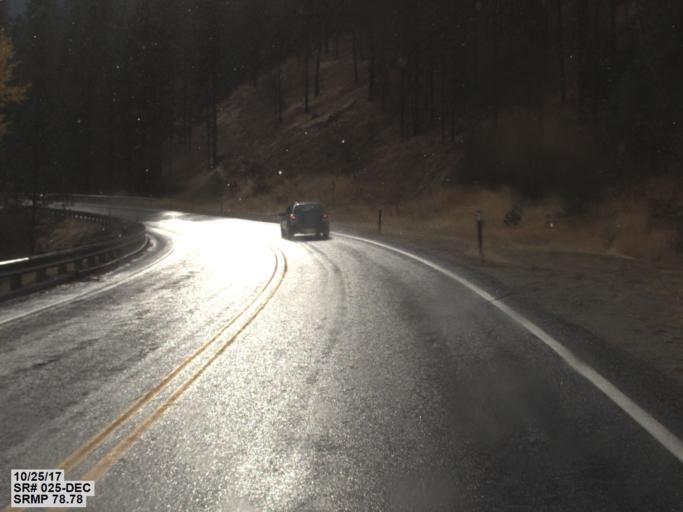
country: US
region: Washington
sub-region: Stevens County
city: Kettle Falls
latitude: 48.5772
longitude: -118.0833
